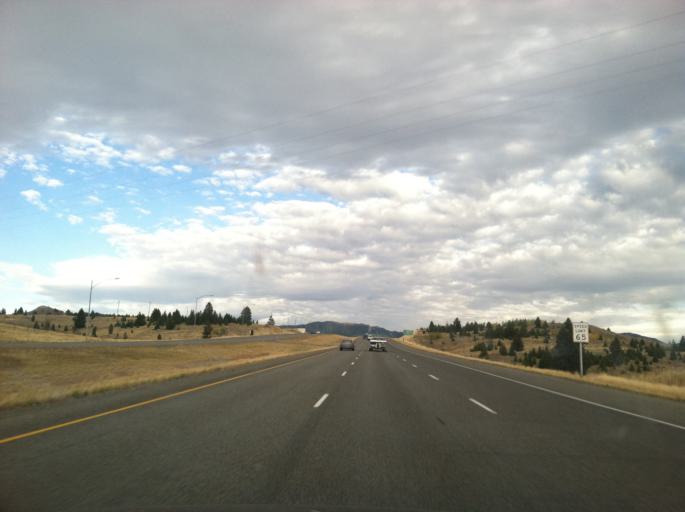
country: US
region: Montana
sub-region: Silver Bow County
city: Butte
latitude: 46.0061
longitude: -112.6021
